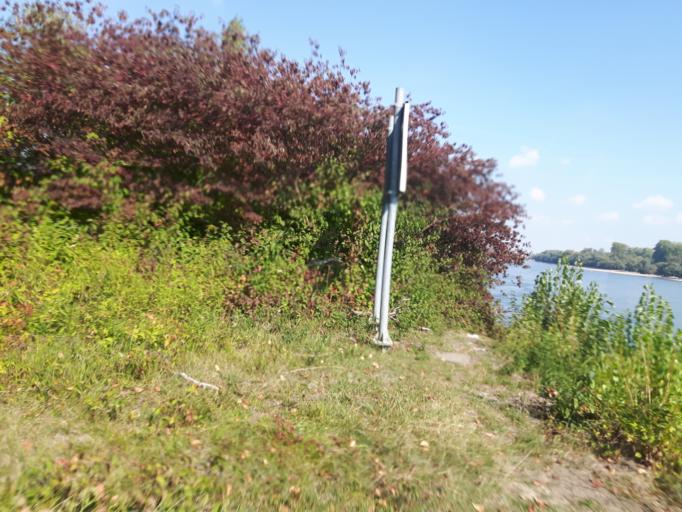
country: DE
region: Rheinland-Pfalz
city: Altrip
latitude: 49.4052
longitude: 8.4946
